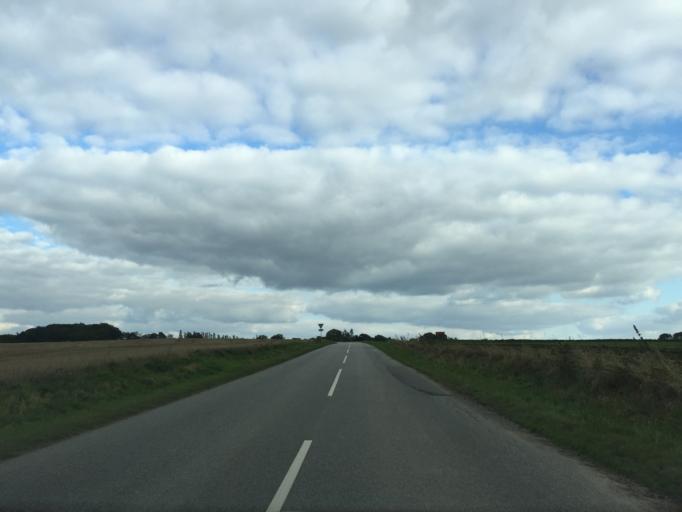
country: DK
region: Central Jutland
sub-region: Favrskov Kommune
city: Ulstrup
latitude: 56.3142
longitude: 9.7767
